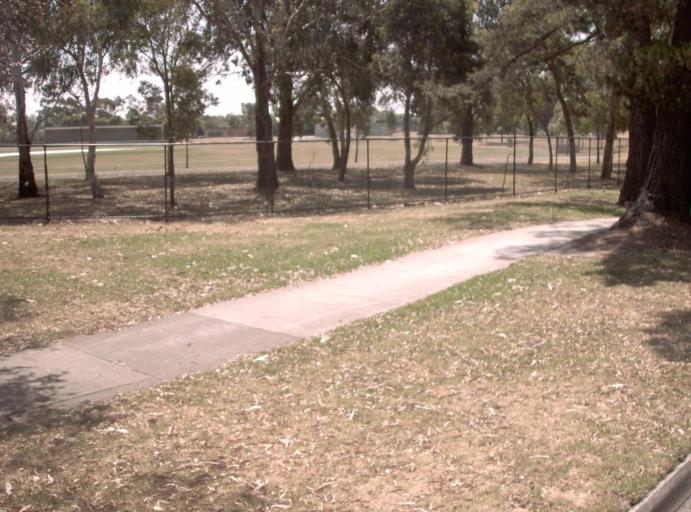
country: AU
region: Victoria
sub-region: Monash
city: Notting Hill
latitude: -37.8928
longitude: 145.1634
